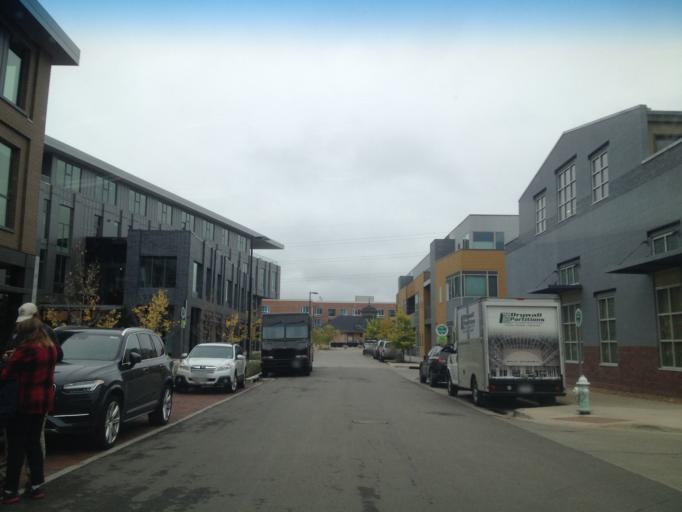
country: US
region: Colorado
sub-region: Boulder County
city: Boulder
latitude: 40.0265
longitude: -105.2510
